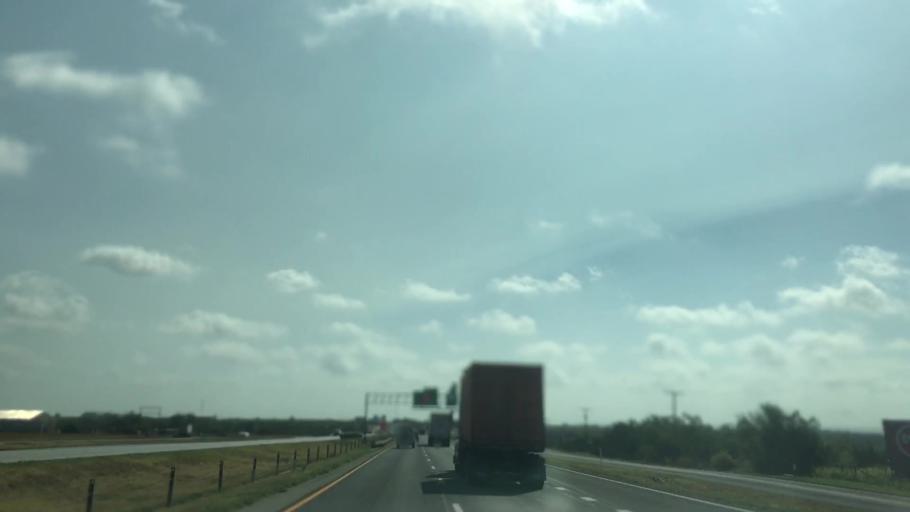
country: US
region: Texas
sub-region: Nolan County
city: Roscoe
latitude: 32.4513
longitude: -100.4785
